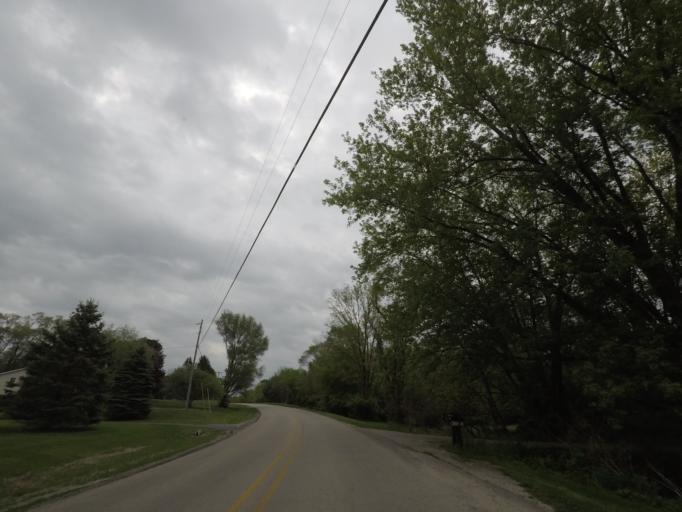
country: US
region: Illinois
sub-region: Winnebago County
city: Roscoe
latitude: 42.4347
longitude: -88.9833
